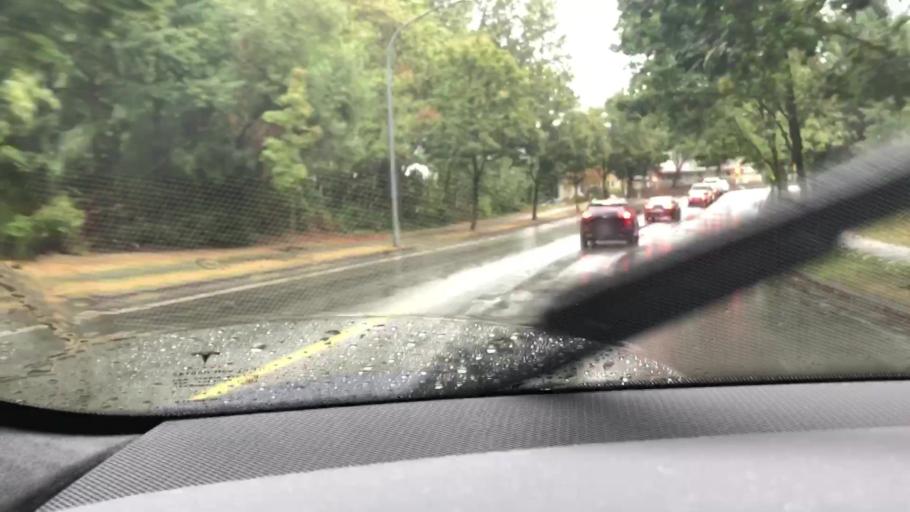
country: CA
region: British Columbia
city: New Westminster
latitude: 49.2387
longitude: -122.9088
